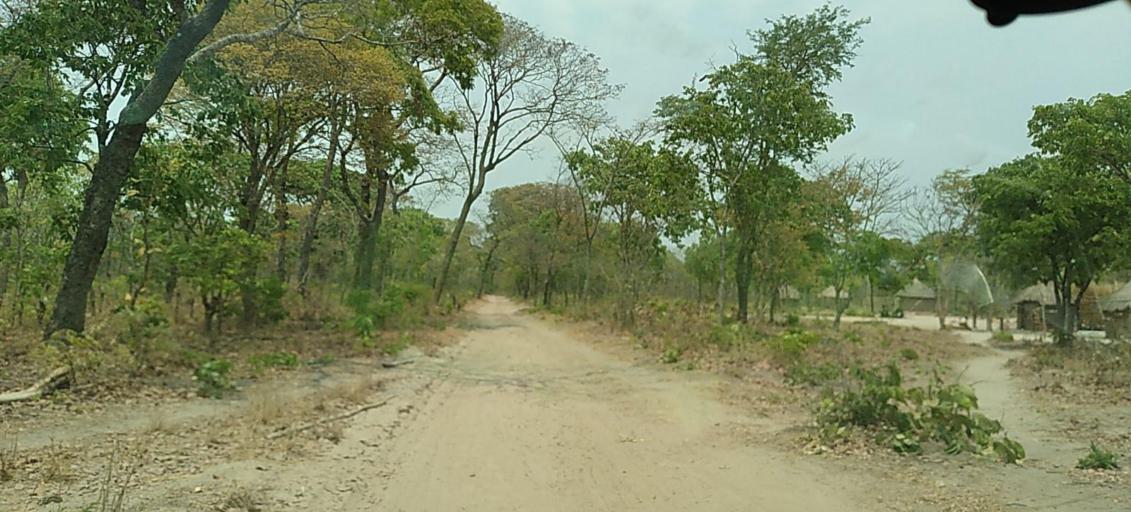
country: ZM
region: North-Western
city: Kabompo
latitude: -13.5435
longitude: 24.4510
